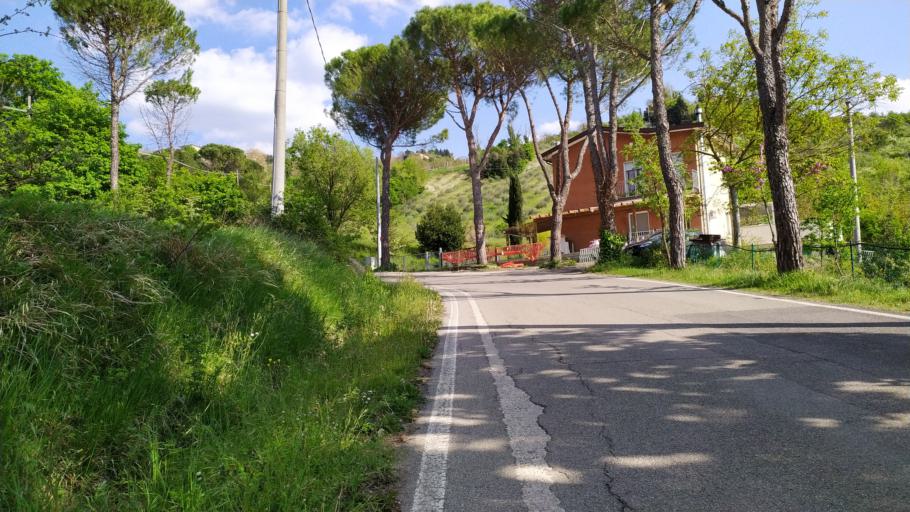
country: IT
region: Emilia-Romagna
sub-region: Provincia di Bologna
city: Borgo Tossignano
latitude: 44.2751
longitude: 11.5962
